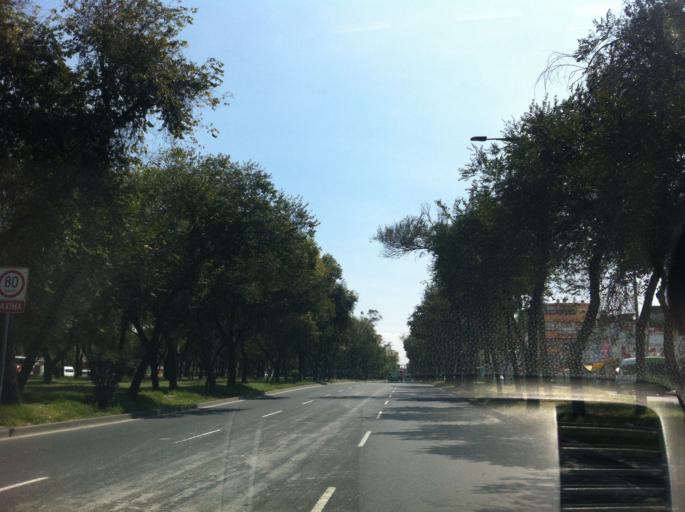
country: MX
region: Mexico City
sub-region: Iztacalco
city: Iztacalco
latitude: 19.4178
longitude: -99.0933
